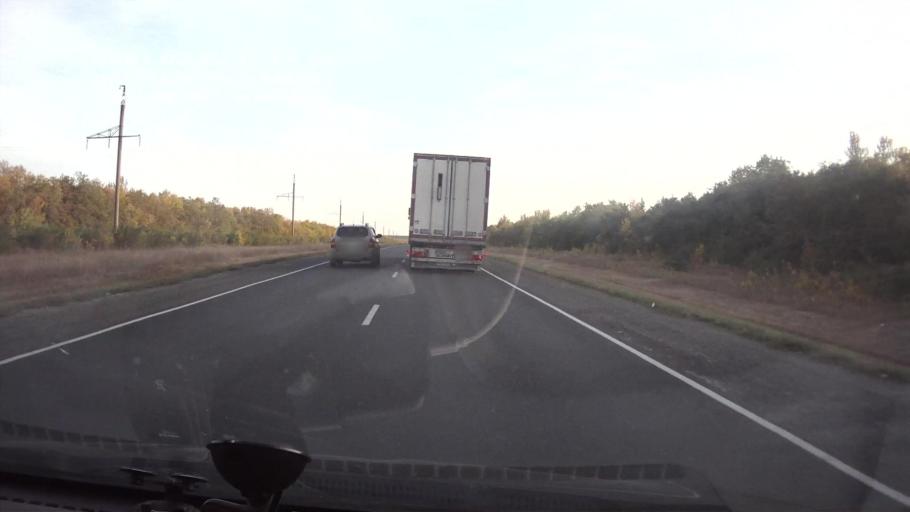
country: RU
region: Saratov
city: Krasnoarmeysk
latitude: 51.1224
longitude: 45.6507
